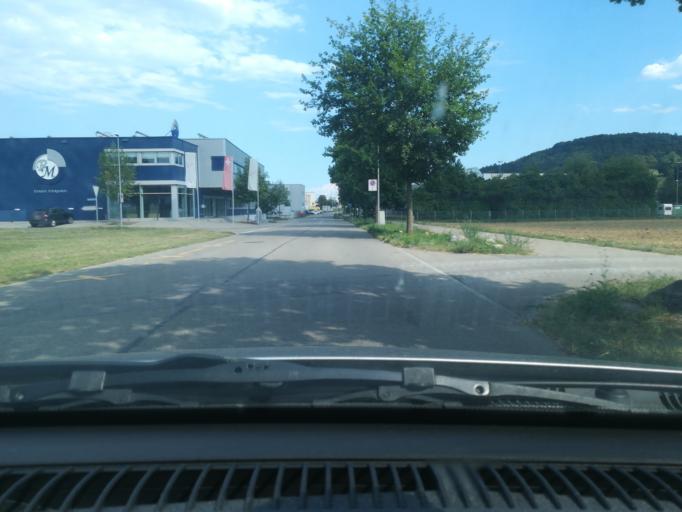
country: CH
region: Schaffhausen
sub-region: Bezirk Reiat
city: Thayngen
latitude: 47.7438
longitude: 8.7067
